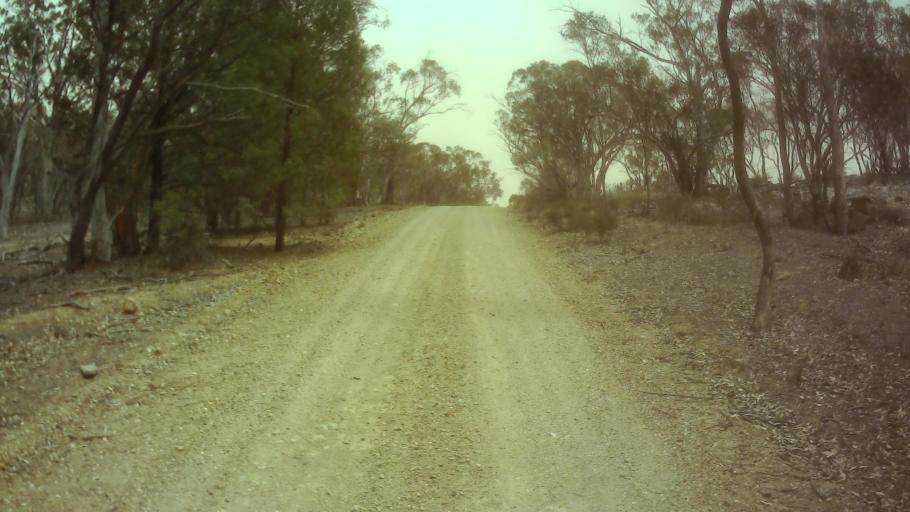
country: AU
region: New South Wales
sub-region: Weddin
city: Grenfell
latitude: -33.7095
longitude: 147.9489
